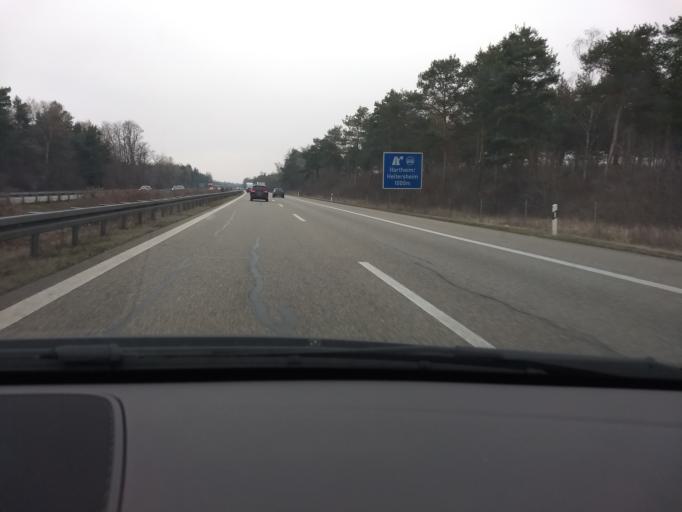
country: FR
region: Alsace
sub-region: Departement du Haut-Rhin
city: Blodelsheim
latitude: 47.8978
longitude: 7.5856
